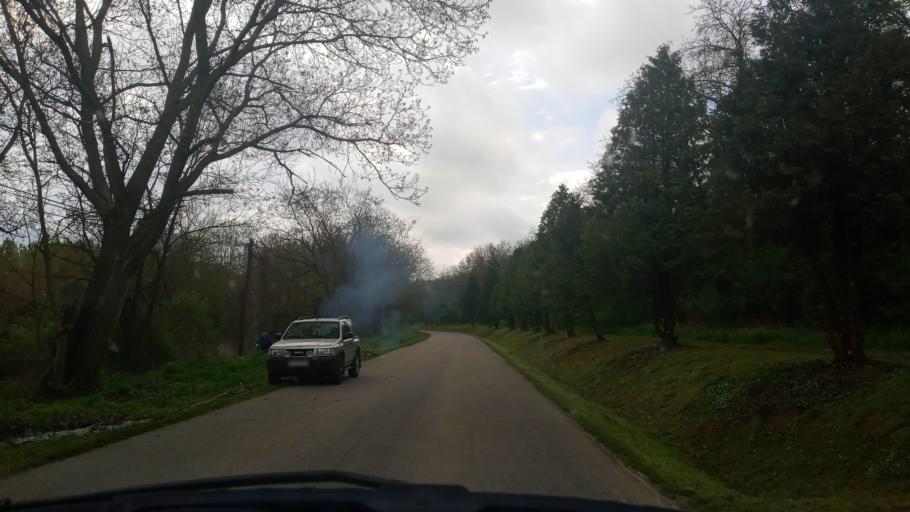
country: HU
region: Baranya
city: Boly
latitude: 45.9909
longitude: 18.4184
